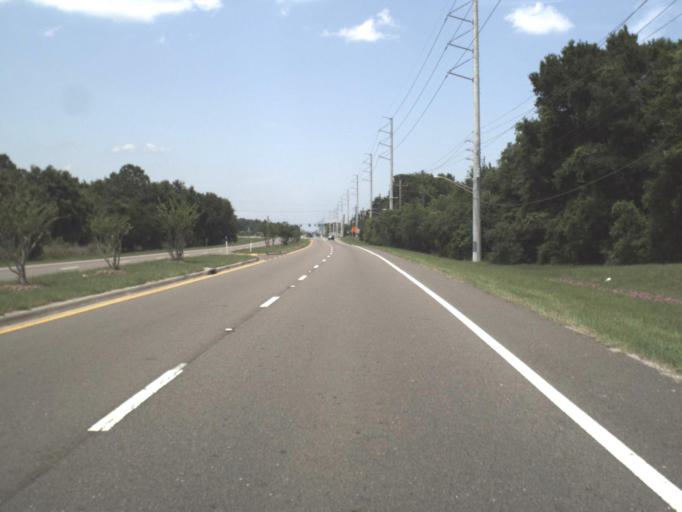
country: US
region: Florida
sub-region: Duval County
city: Jacksonville
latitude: 30.4259
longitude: -81.6462
